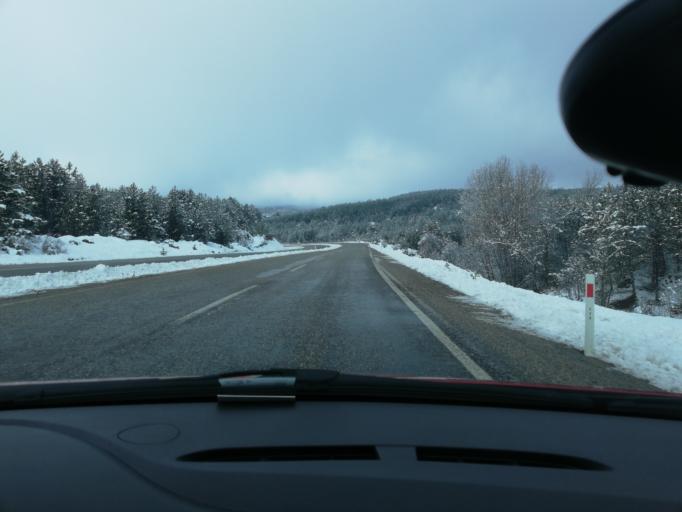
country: TR
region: Kastamonu
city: Ihsangazi
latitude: 41.3038
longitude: 33.5561
